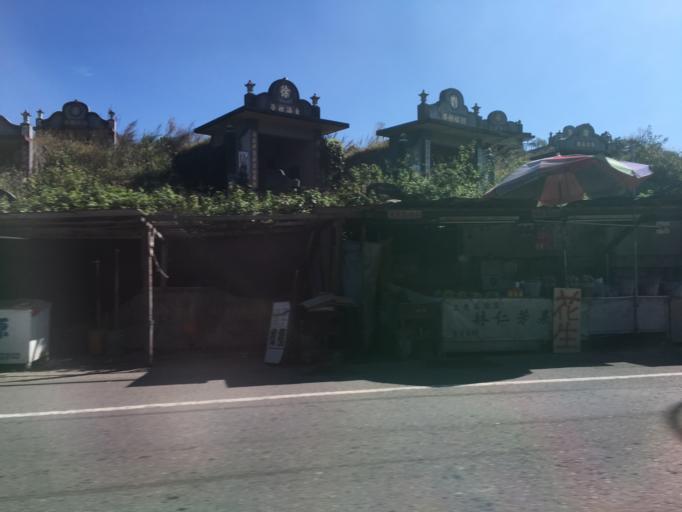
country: TW
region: Taiwan
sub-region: Hsinchu
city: Hsinchu
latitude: 24.6497
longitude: 120.9541
